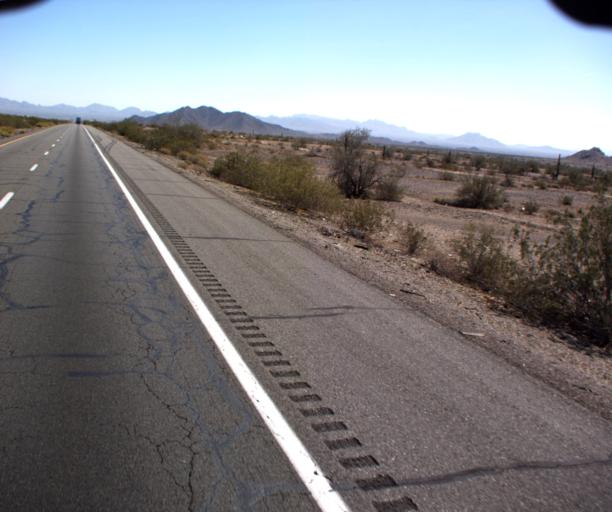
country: US
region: Arizona
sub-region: La Paz County
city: Quartzsite
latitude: 33.6487
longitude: -114.3174
